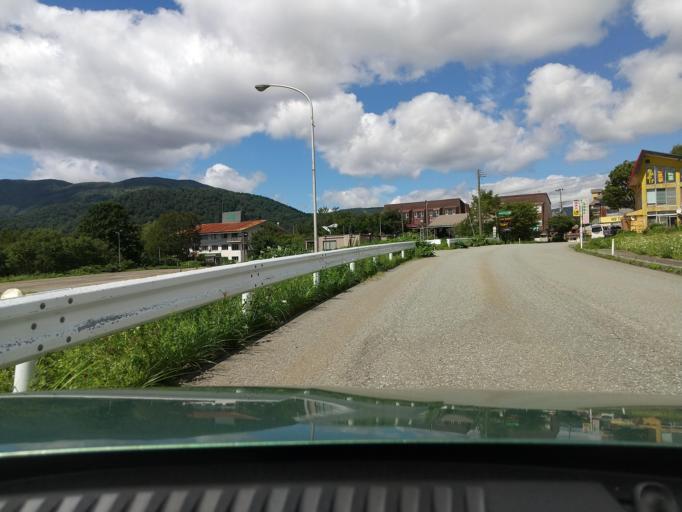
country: JP
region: Iwate
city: Shizukuishi
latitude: 39.7779
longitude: 140.7619
